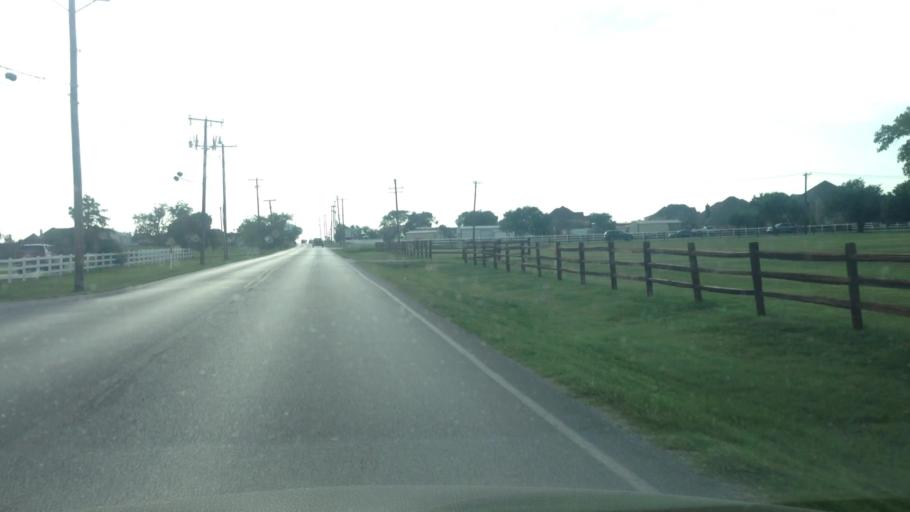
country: US
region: Texas
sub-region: Tarrant County
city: Haslet
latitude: 32.9689
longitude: -97.3964
